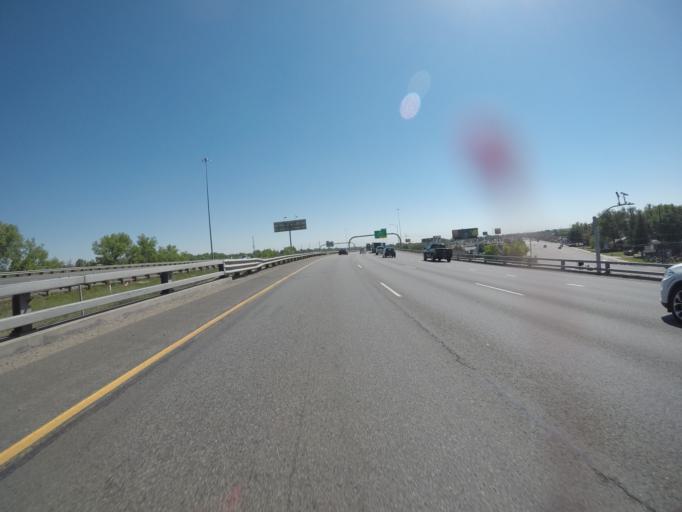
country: US
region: Colorado
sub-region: Jefferson County
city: Applewood
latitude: 39.7785
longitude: -105.1408
